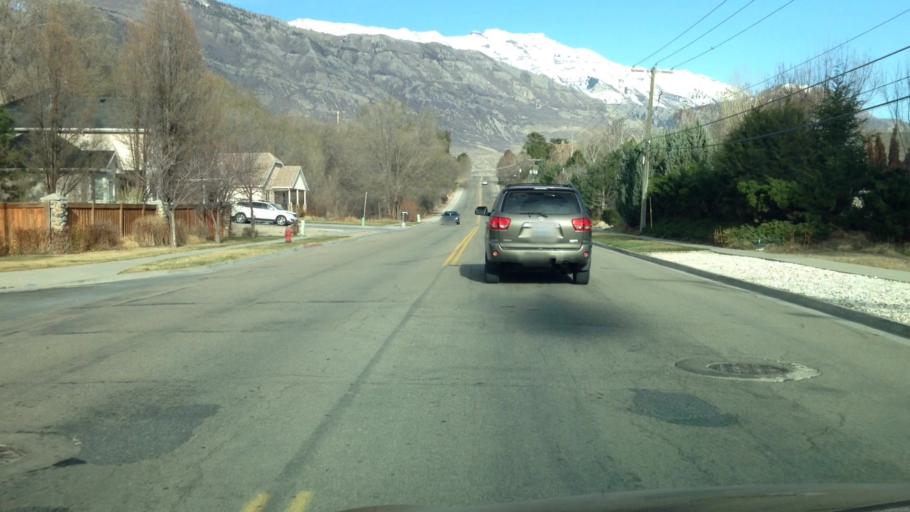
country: US
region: Utah
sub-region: Utah County
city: American Fork
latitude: 40.3919
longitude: -111.7794
